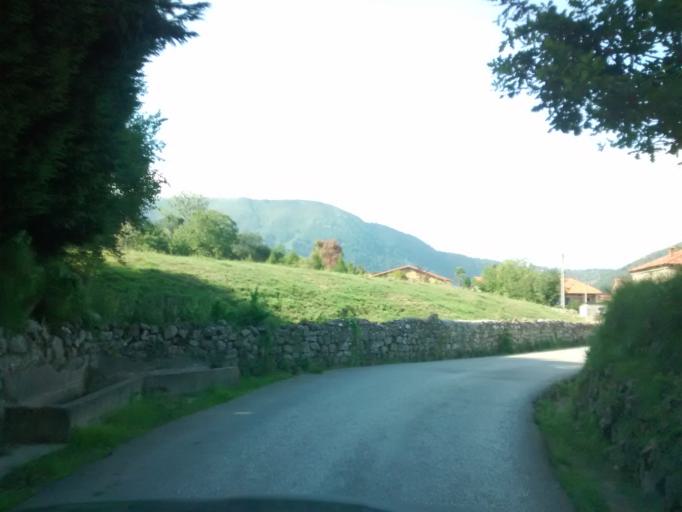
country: ES
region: Cantabria
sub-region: Provincia de Cantabria
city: Ruente
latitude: 43.2564
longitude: -4.2467
